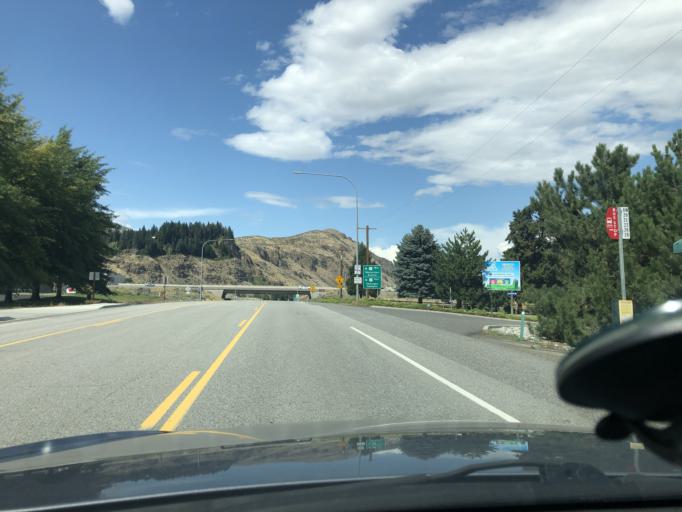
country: US
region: Washington
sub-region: Chelan County
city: Sunnyslope
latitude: 47.4695
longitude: -120.3247
